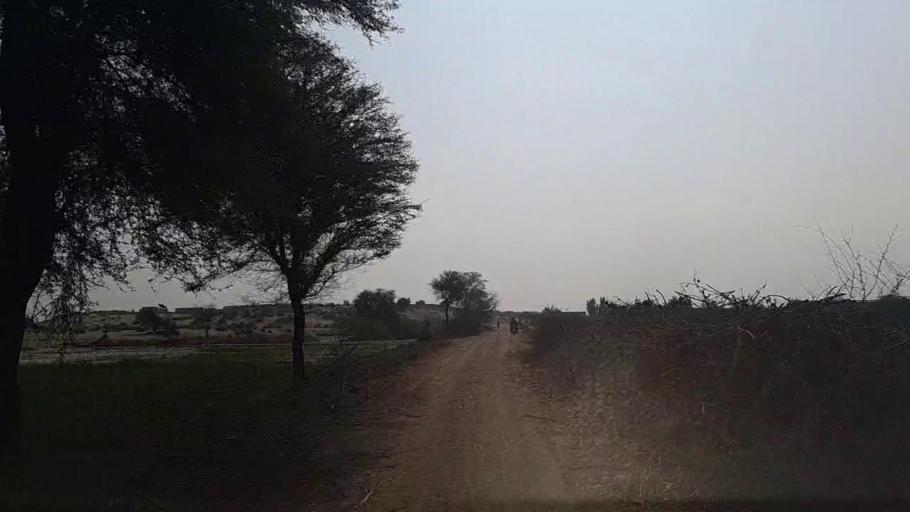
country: PK
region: Sindh
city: Jam Sahib
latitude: 26.4342
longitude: 68.5341
